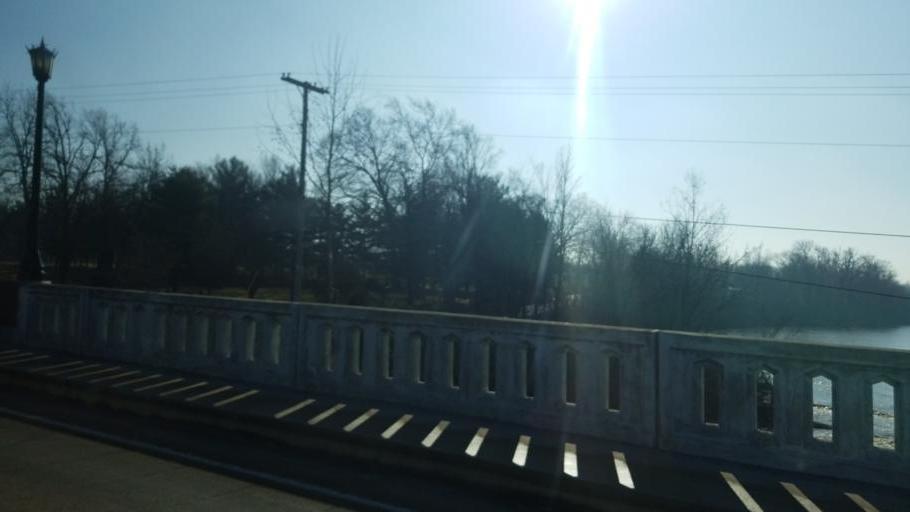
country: US
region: Ohio
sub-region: Seneca County
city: Tiffin
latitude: 41.1310
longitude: -83.1658
